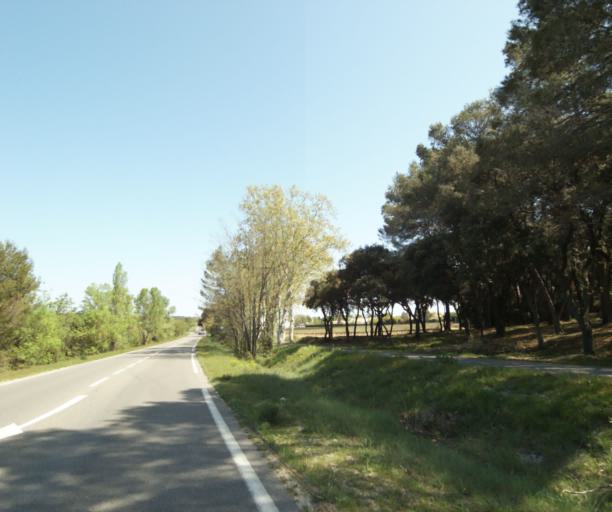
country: FR
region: Languedoc-Roussillon
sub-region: Departement de l'Herault
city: Clapiers
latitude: 43.6540
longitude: 3.8979
